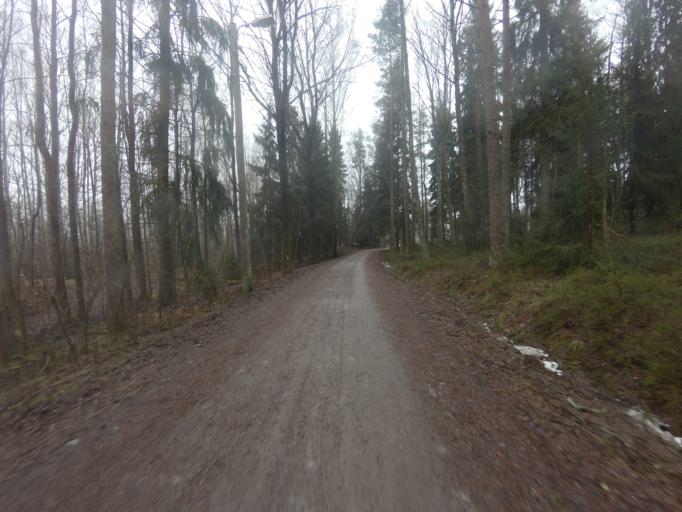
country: FI
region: Uusimaa
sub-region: Helsinki
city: Espoo
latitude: 60.1552
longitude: 24.6934
